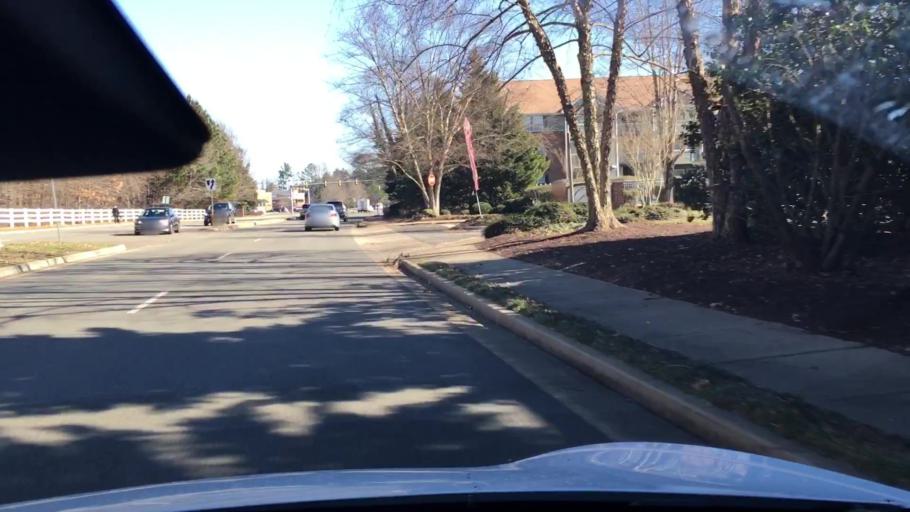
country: US
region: Virginia
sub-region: Henrico County
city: Glen Allen
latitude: 37.6657
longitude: -77.4631
